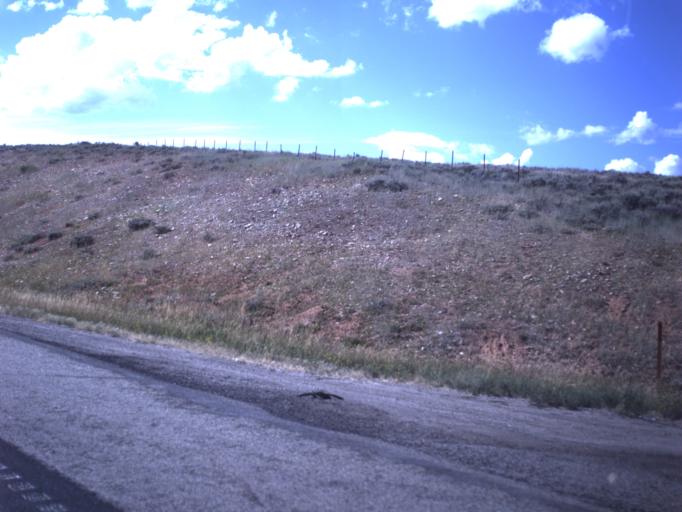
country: US
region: Utah
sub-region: Wasatch County
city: Heber
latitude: 40.2306
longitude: -111.1225
